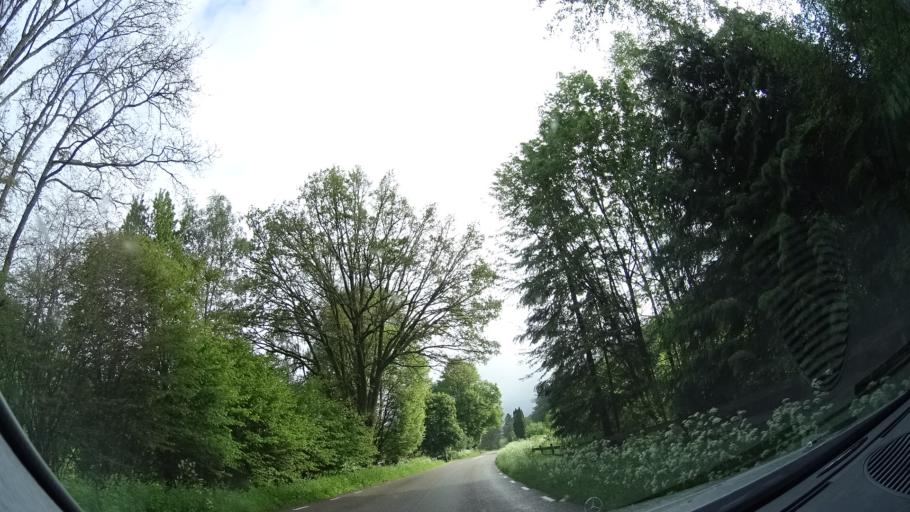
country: SE
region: Skane
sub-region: Hoors Kommun
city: Hoeoer
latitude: 55.9605
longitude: 13.4564
